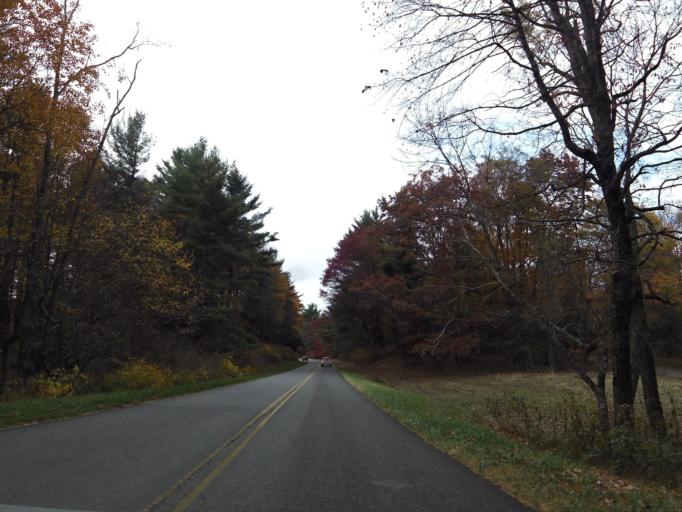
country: US
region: Virginia
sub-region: Carroll County
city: Cana
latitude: 36.6244
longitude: -80.7587
